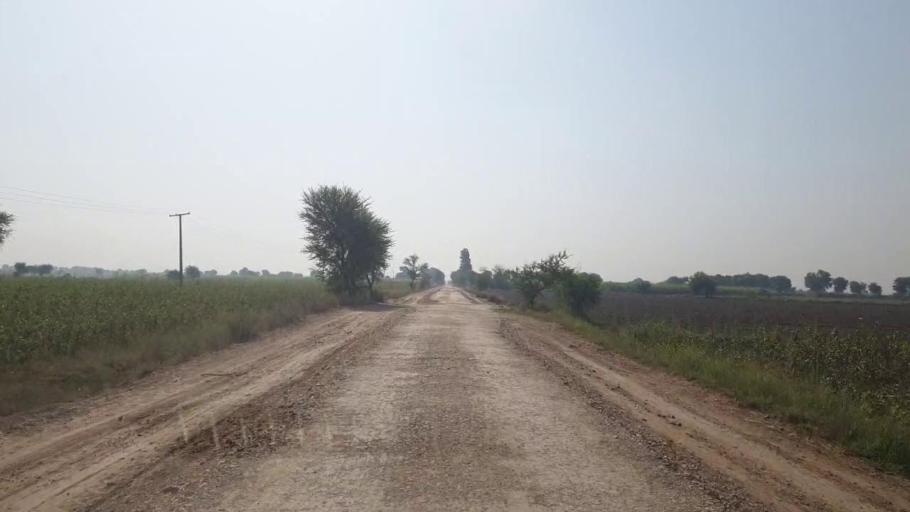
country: PK
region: Sindh
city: Shahdadpur
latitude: 25.9122
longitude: 68.7408
